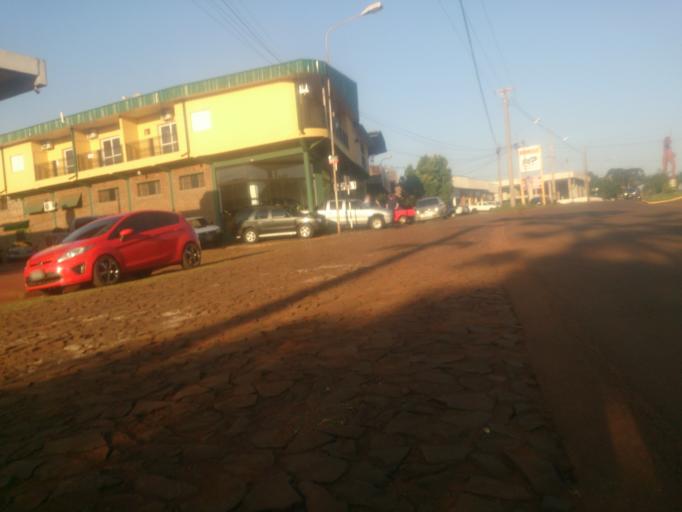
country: AR
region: Misiones
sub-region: Departamento de Obera
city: Obera
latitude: -27.4760
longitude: -55.0977
